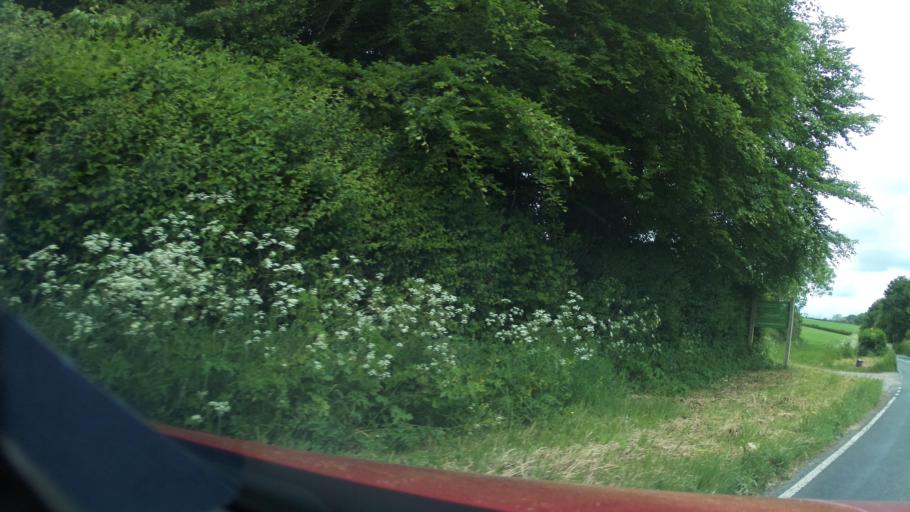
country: GB
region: England
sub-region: Dorset
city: Dorchester
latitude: 50.7551
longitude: -2.4738
